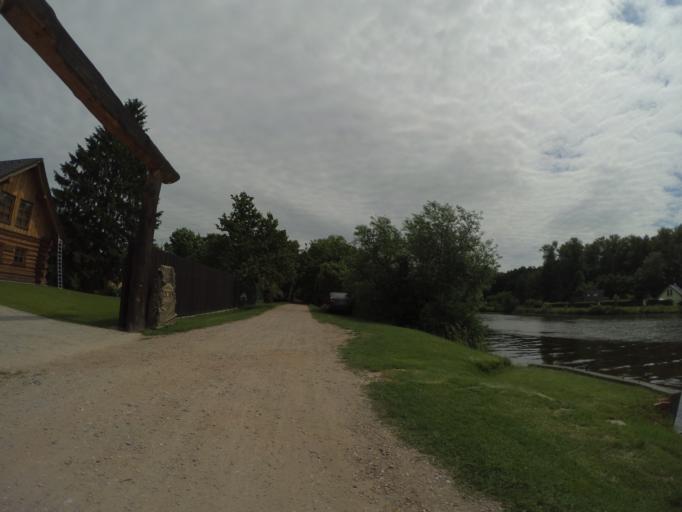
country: CZ
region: Central Bohemia
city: Prerov nad Labem
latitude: 50.1745
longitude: 14.8605
